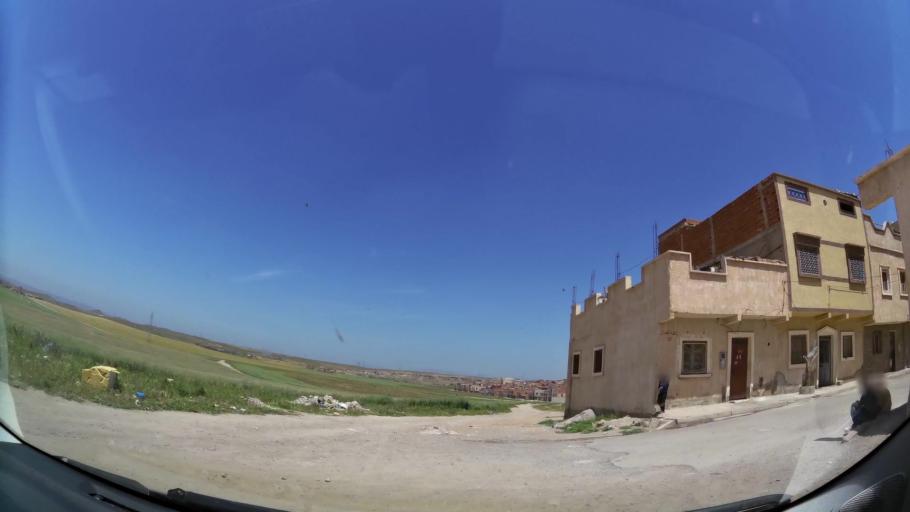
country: MA
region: Oriental
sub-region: Oujda-Angad
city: Oujda
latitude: 34.6872
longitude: -1.9559
